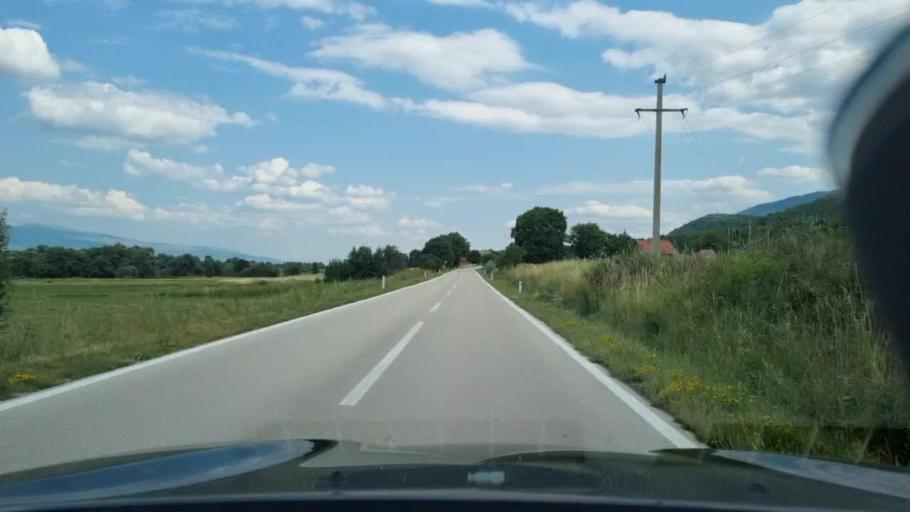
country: HR
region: Splitsko-Dalmatinska
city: Hrvace
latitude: 43.9950
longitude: 16.6162
